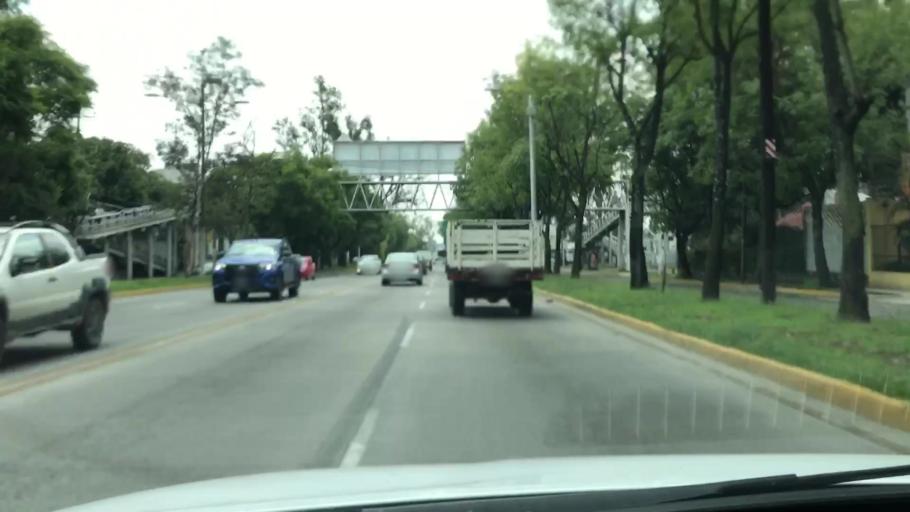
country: MX
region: Jalisco
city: Zapopan2
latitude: 20.6892
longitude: -103.4475
